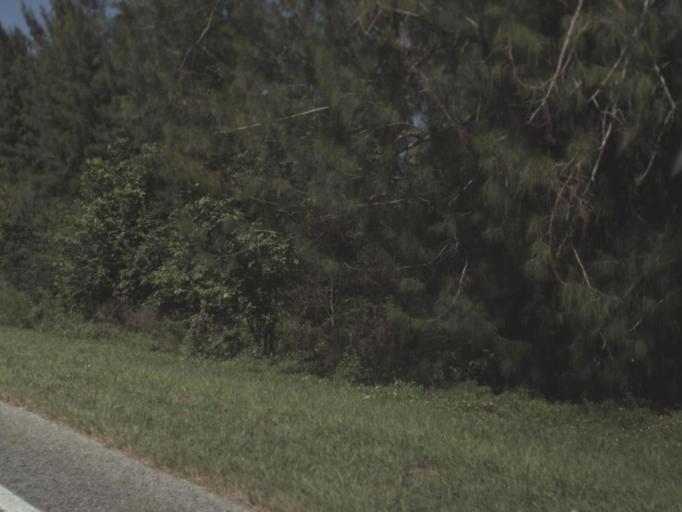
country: US
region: Florida
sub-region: Hendry County
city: Clewiston
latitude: 26.7536
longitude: -80.9084
